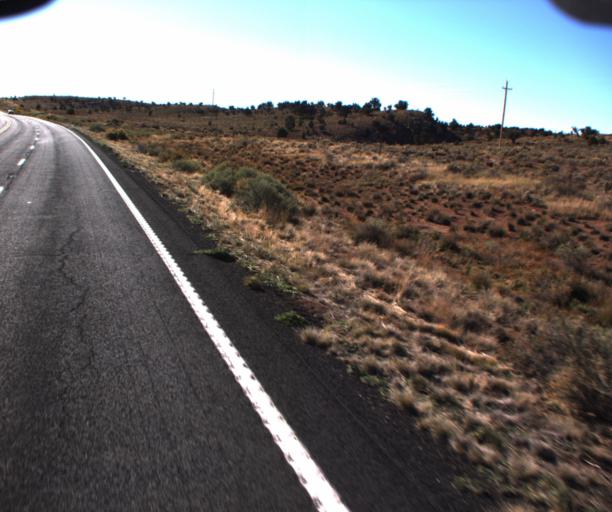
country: US
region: Arizona
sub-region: Coconino County
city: Tuba City
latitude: 36.4022
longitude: -111.5332
